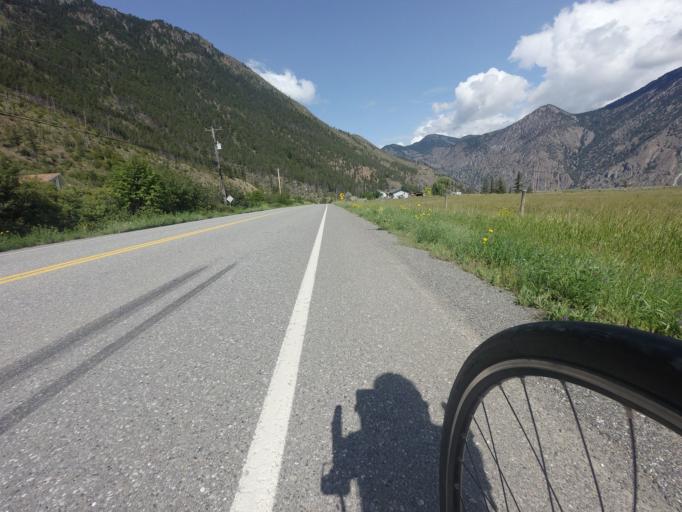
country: CA
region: British Columbia
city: Lillooet
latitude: 50.7429
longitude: -121.8857
